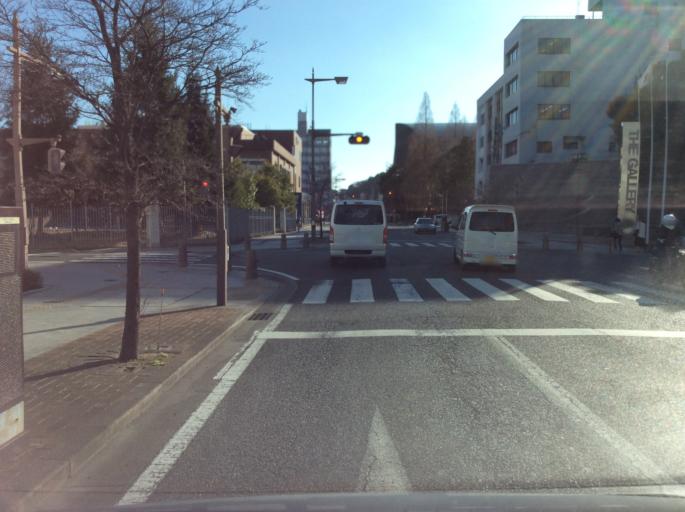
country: JP
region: Fukushima
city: Iwaki
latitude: 37.0523
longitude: 140.8903
